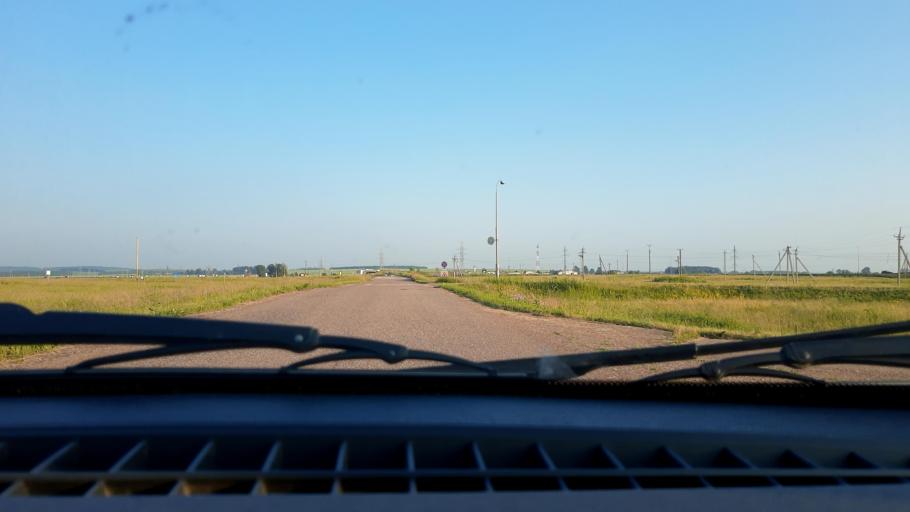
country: RU
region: Bashkortostan
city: Asanovo
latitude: 54.9061
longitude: 55.6273
